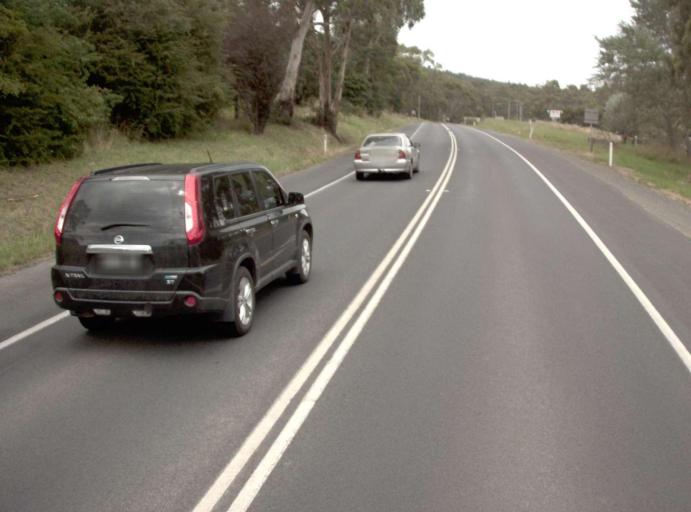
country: AU
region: Victoria
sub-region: Yarra Ranges
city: Lilydale
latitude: -37.7445
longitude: 145.3734
